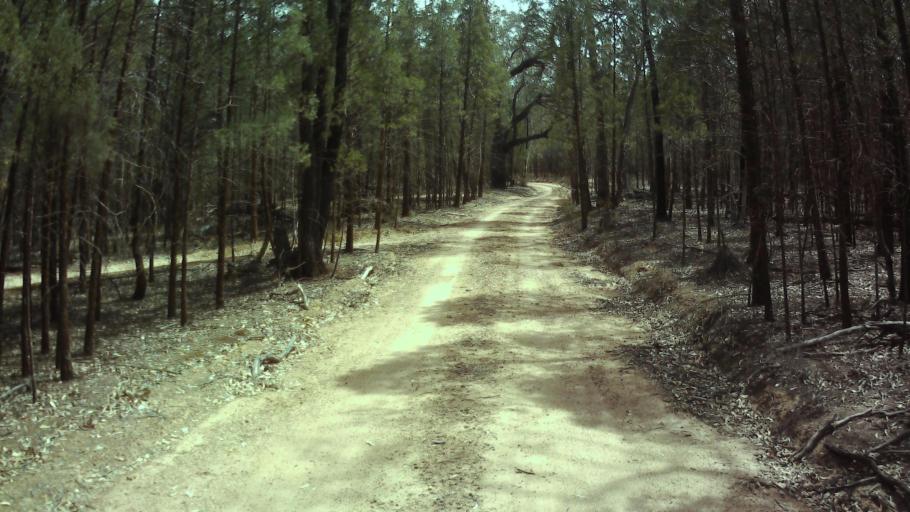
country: AU
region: New South Wales
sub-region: Weddin
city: Grenfell
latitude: -33.8874
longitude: 148.3828
